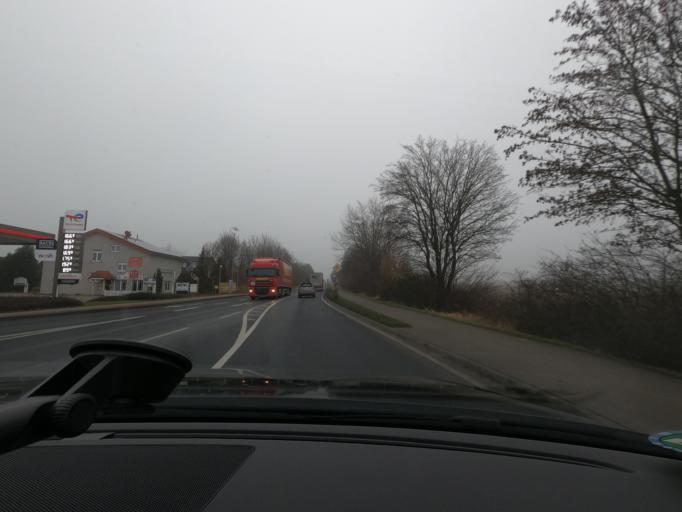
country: DE
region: North Rhine-Westphalia
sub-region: Regierungsbezirk Koln
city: Merzenich
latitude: 50.8195
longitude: 6.5331
